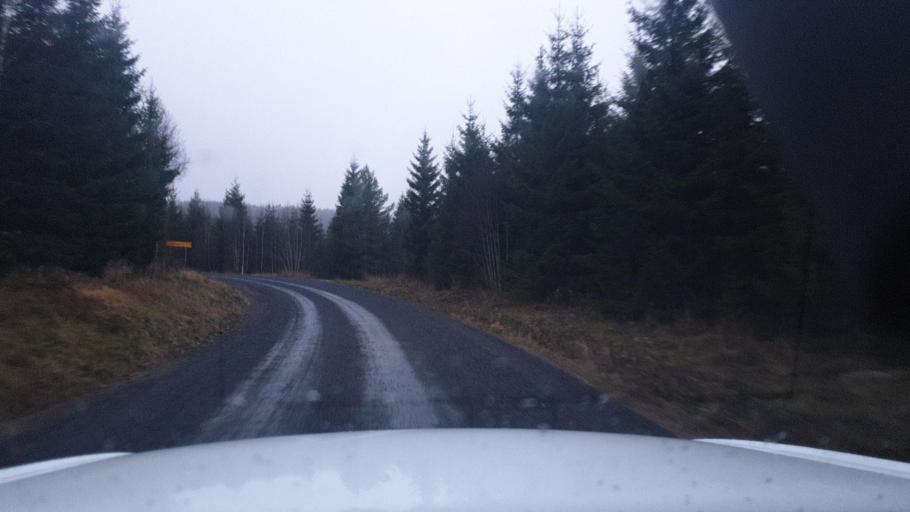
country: SE
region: Vaermland
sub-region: Torsby Kommun
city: Torsby
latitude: 60.1862
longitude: 12.6466
